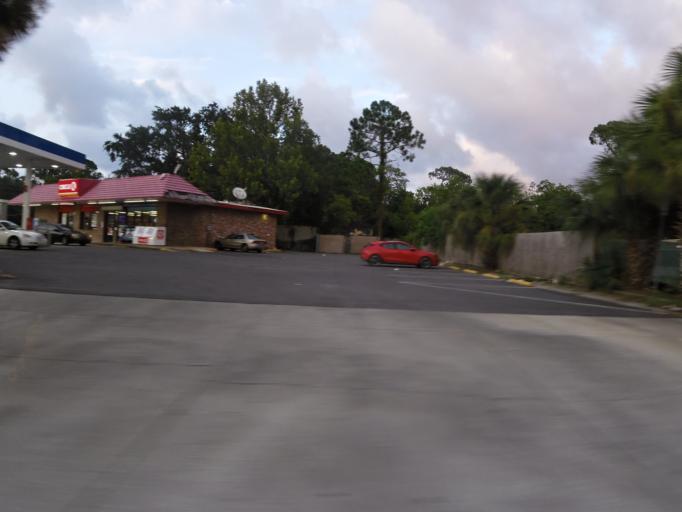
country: US
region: Florida
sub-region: Duval County
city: Jacksonville
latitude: 30.3120
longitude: -81.7177
